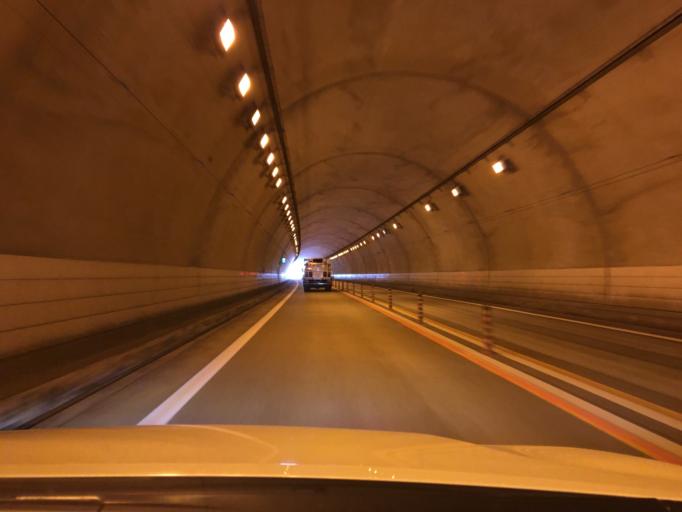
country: JP
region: Yamagata
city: Sagae
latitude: 38.4380
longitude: 140.1276
